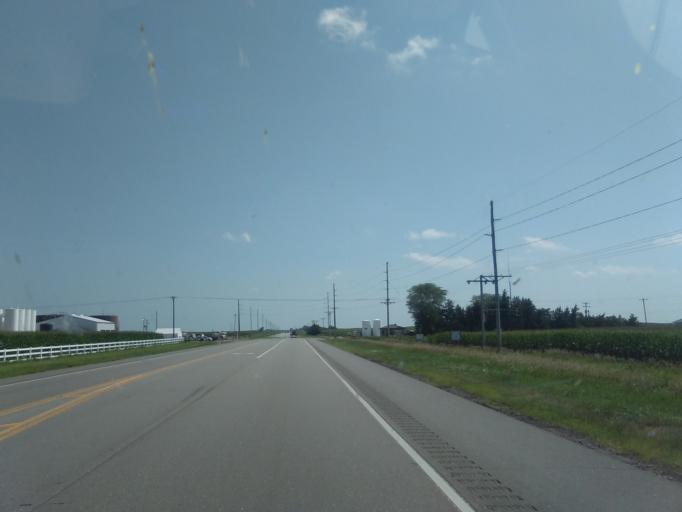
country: US
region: Nebraska
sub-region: Phelps County
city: Holdrege
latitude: 40.6593
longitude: -99.3804
